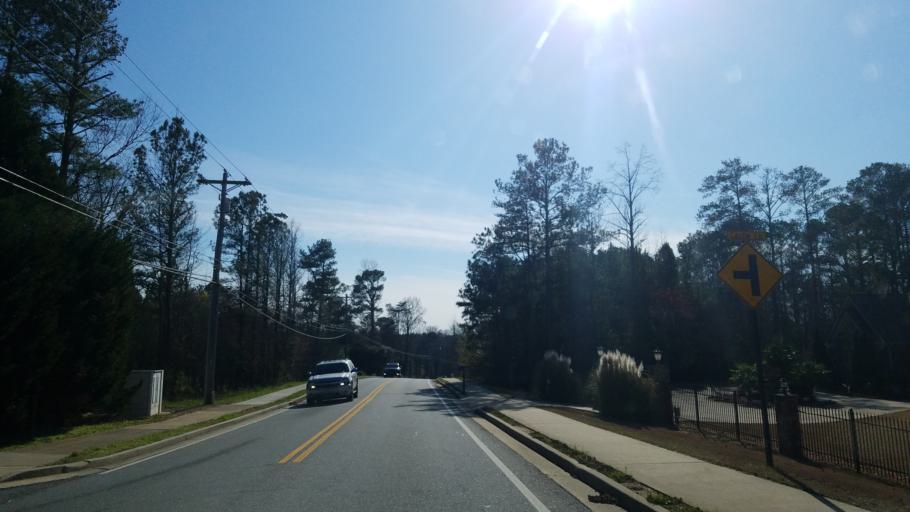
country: US
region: Georgia
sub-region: Fulton County
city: Roswell
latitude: 34.0141
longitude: -84.4445
